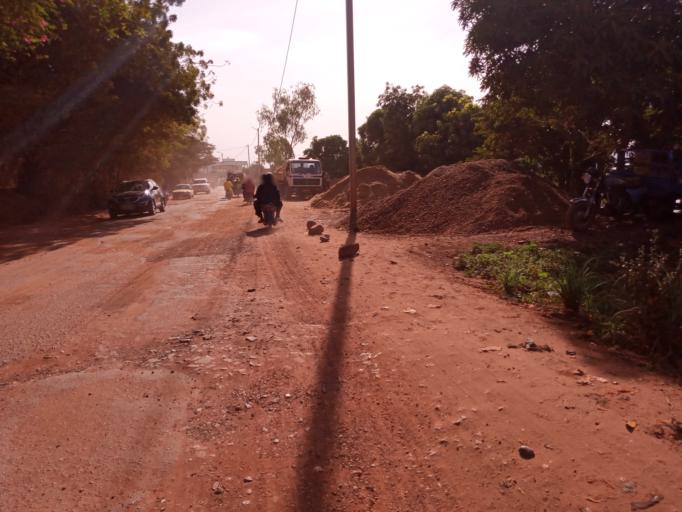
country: ML
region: Bamako
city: Bamako
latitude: 12.6278
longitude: -7.9540
